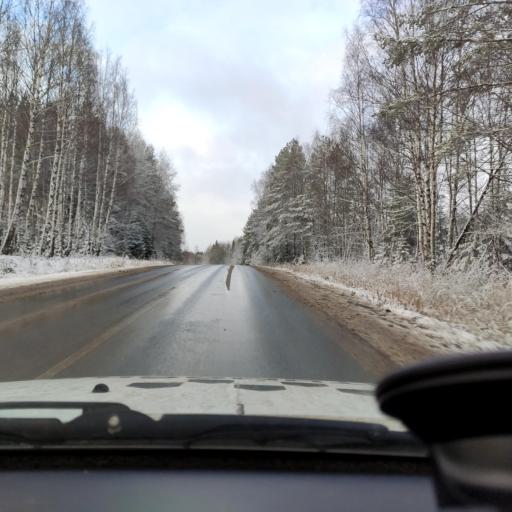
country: RU
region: Perm
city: Nytva
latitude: 57.9309
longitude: 55.3894
